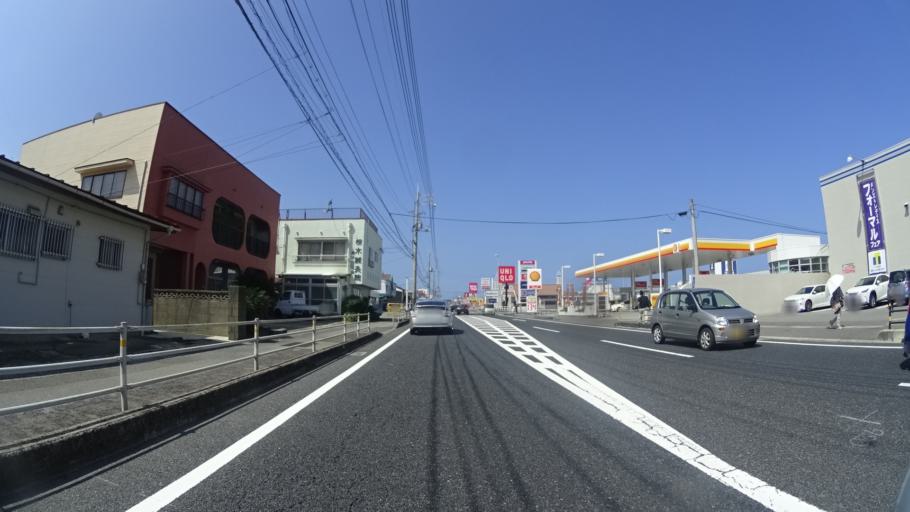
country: JP
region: Shimane
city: Masuda
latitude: 34.6894
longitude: 131.8192
